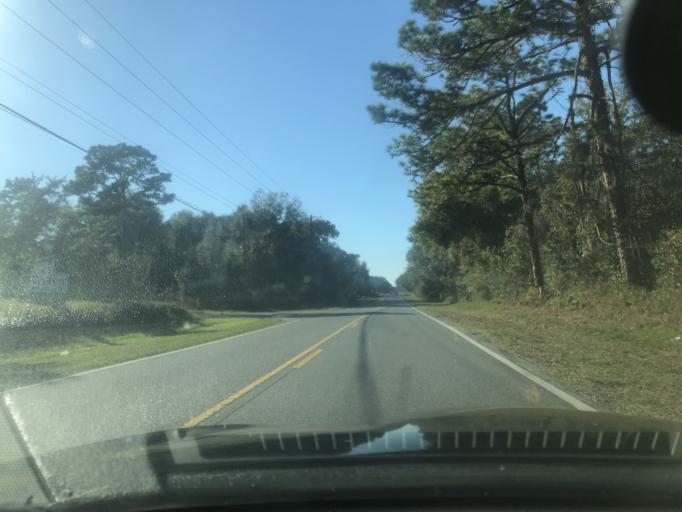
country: US
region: Florida
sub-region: Citrus County
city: Homosassa Springs
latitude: 28.8185
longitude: -82.5373
